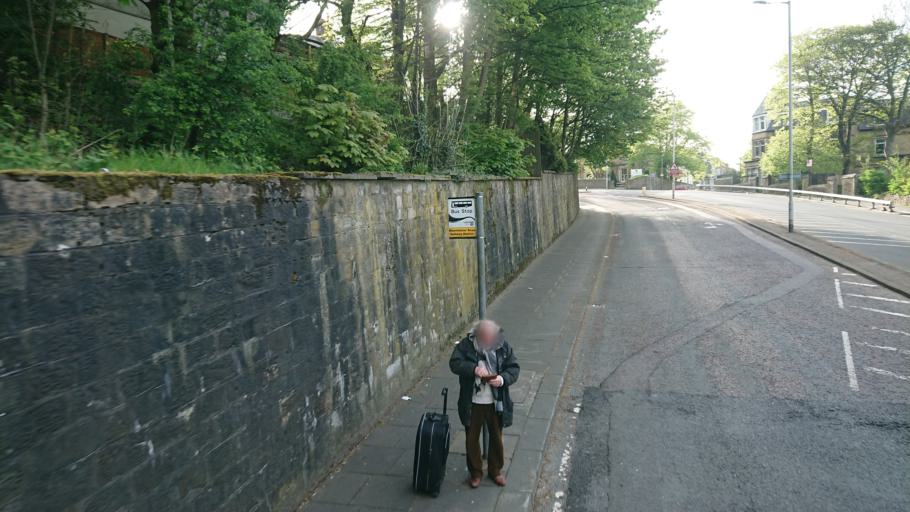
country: GB
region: England
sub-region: Lancashire
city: Burnley
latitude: 53.7847
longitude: -2.2491
